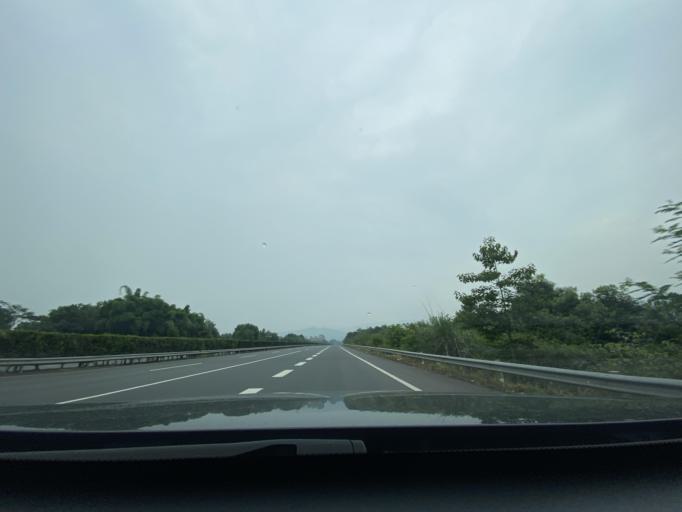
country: CN
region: Sichuan
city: Longquan
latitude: 30.3447
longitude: 104.1259
